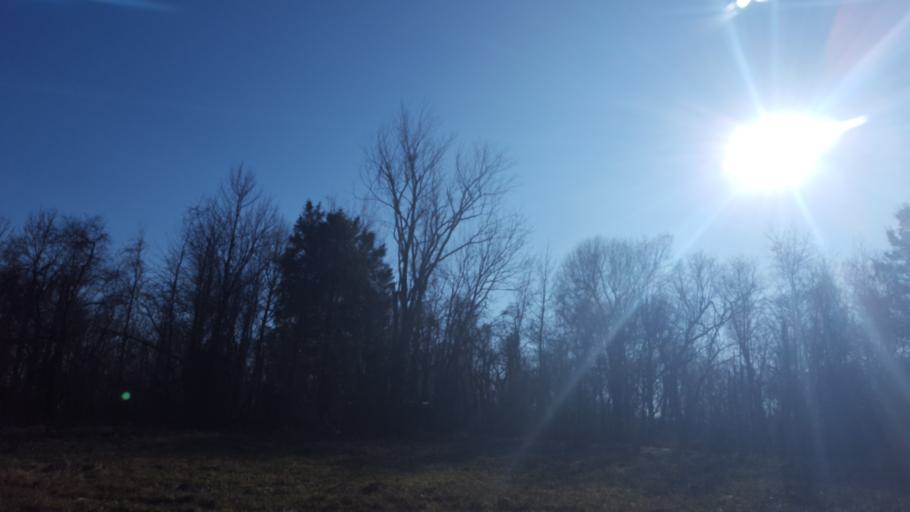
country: US
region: Kentucky
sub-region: Crittenden County
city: Marion
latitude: 37.4509
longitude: -88.0747
